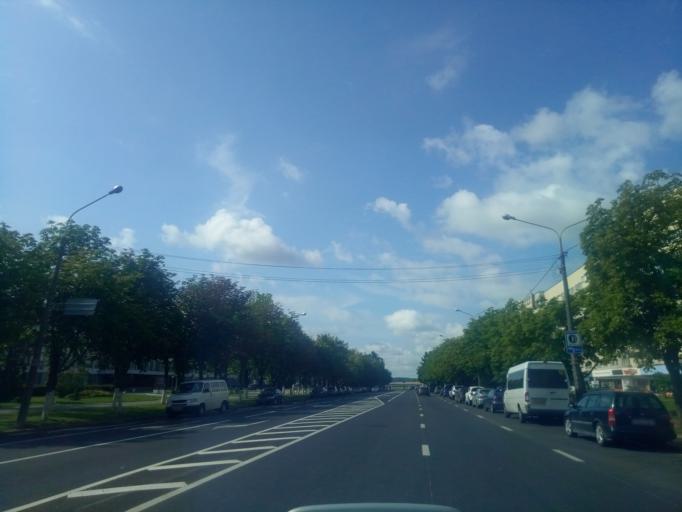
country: BY
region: Minsk
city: Yubilyeyny
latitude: 53.8434
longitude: 27.5054
